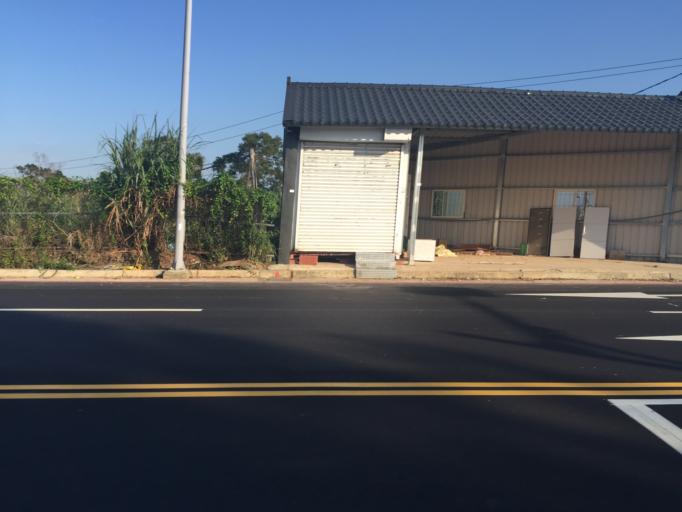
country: TW
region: Taiwan
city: Taoyuan City
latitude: 24.9420
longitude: 121.2644
